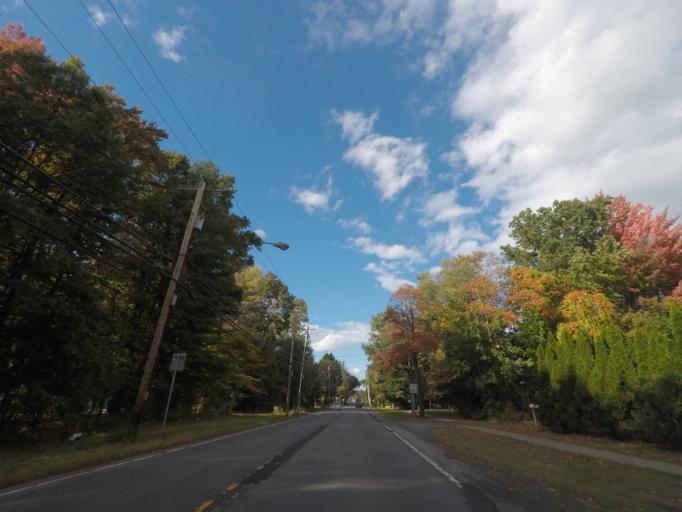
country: US
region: New York
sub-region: Schenectady County
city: Rotterdam
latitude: 42.7363
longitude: -73.9401
